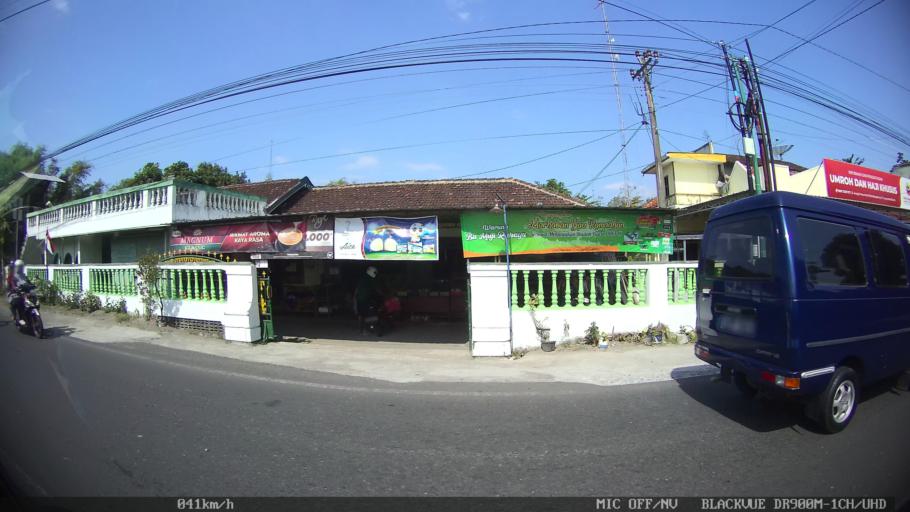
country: ID
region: Daerah Istimewa Yogyakarta
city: Sewon
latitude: -7.8939
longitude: 110.3853
